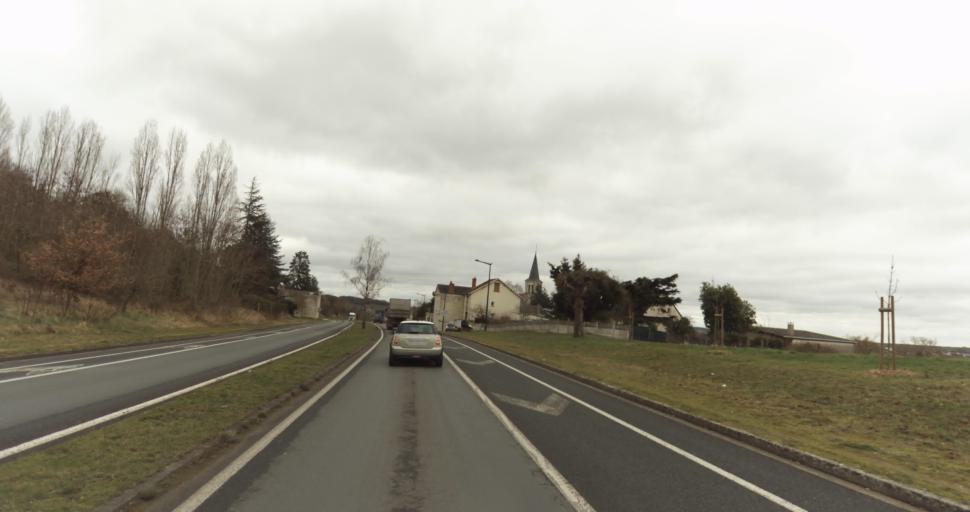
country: FR
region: Pays de la Loire
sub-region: Departement de Maine-et-Loire
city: Varrains
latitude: 47.2277
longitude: -0.0690
